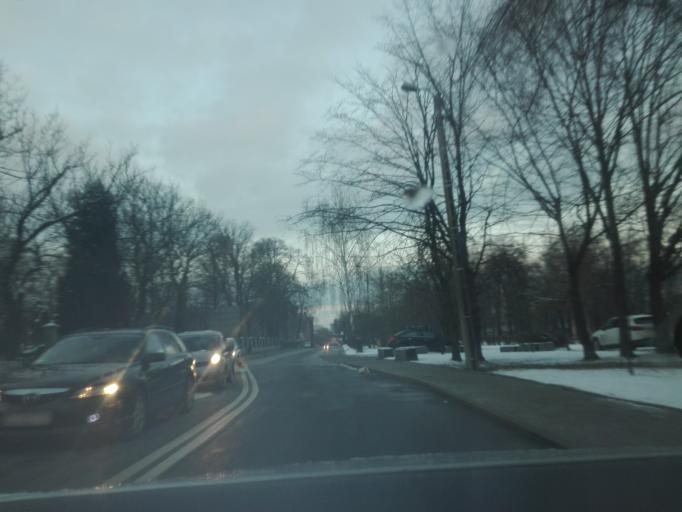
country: PL
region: Silesian Voivodeship
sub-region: Katowice
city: Katowice
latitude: 50.2520
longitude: 19.0299
